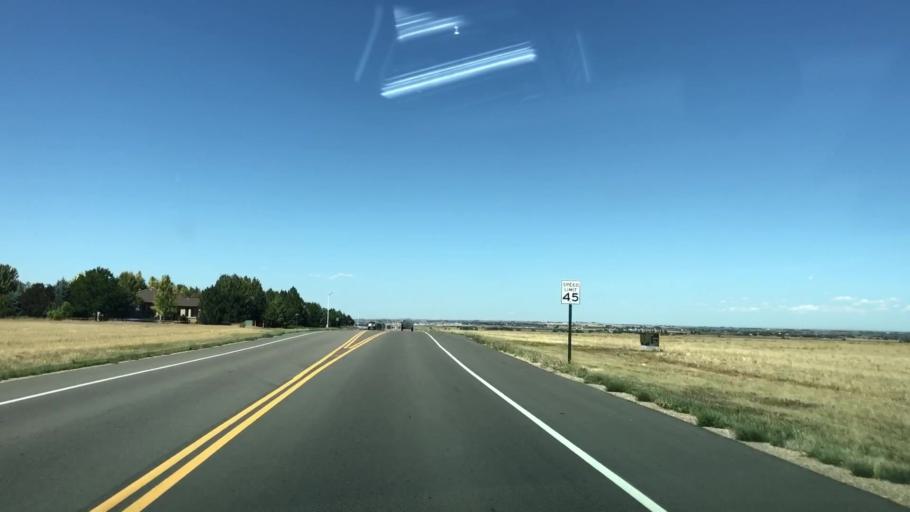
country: US
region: Colorado
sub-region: Weld County
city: Windsor
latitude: 40.4599
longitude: -104.9441
